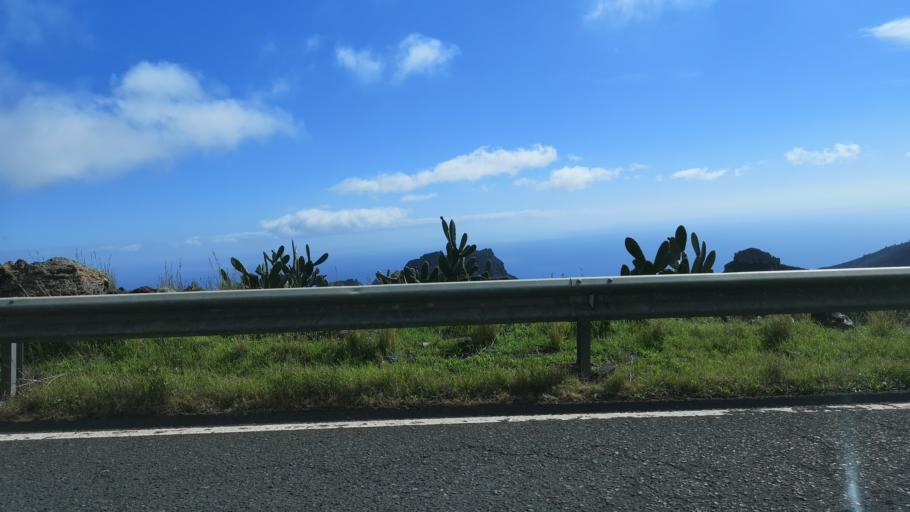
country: ES
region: Canary Islands
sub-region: Provincia de Santa Cruz de Tenerife
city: Alajero
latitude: 28.0986
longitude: -17.1880
